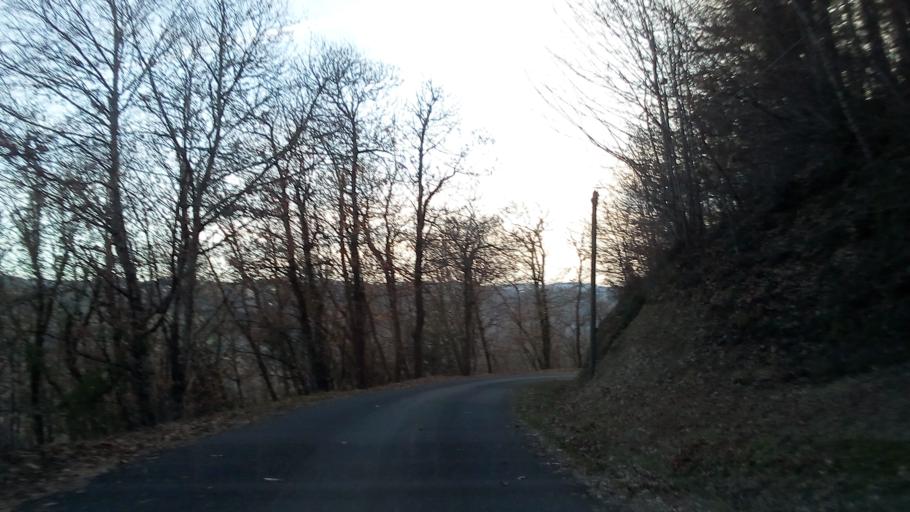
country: FR
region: Limousin
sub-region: Departement de la Correze
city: Naves
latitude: 45.3052
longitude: 1.7810
